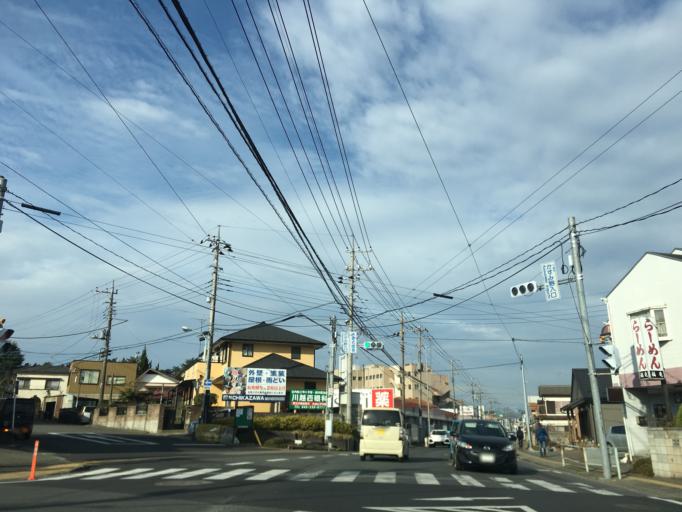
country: JP
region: Saitama
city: Sakado
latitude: 35.9083
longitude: 139.4150
